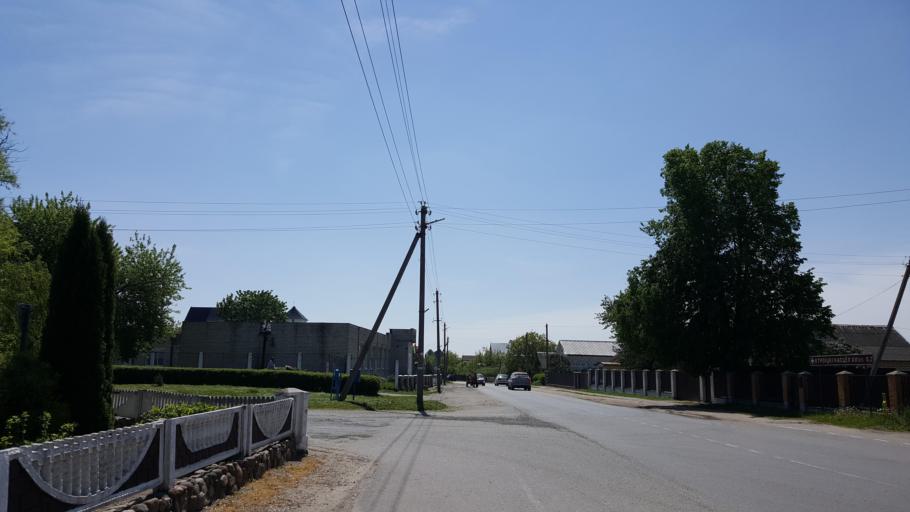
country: BY
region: Brest
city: Charnawchytsy
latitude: 52.2198
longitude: 23.7397
